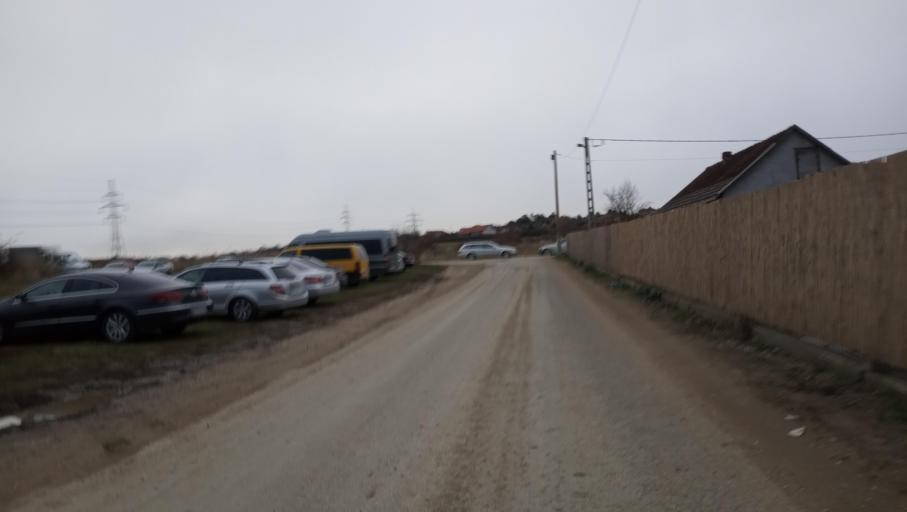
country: HU
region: Pest
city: Urom
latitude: 47.5988
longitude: 19.0241
